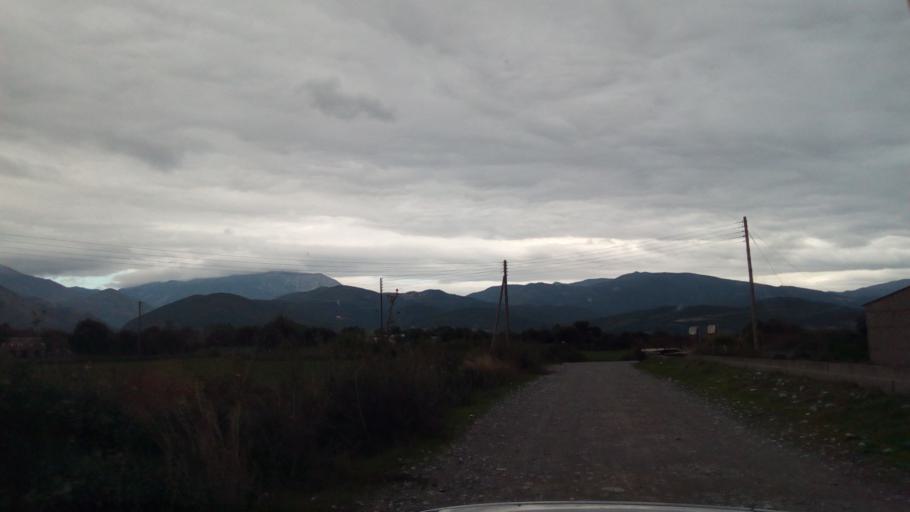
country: GR
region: West Greece
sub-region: Nomos Aitolias kai Akarnanias
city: Nafpaktos
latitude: 38.3888
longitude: 21.8869
